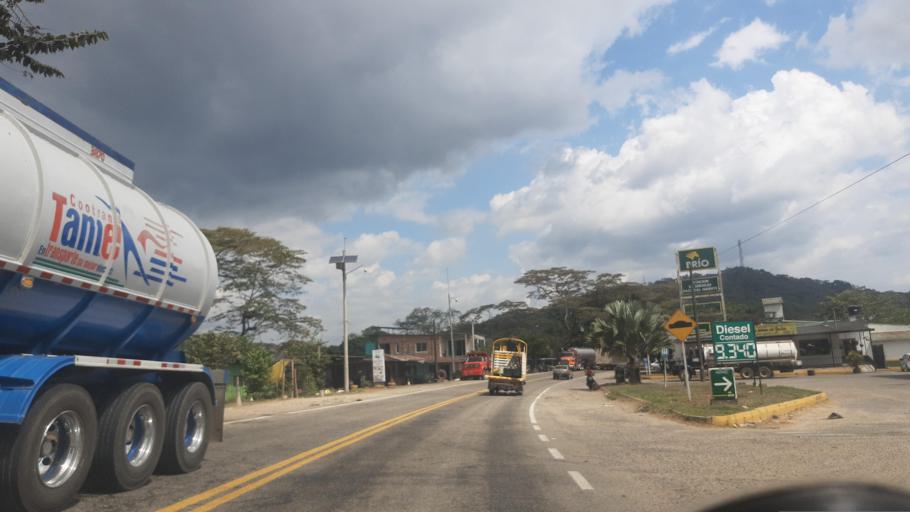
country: CO
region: Casanare
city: Tauramena
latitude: 5.0072
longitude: -72.6899
